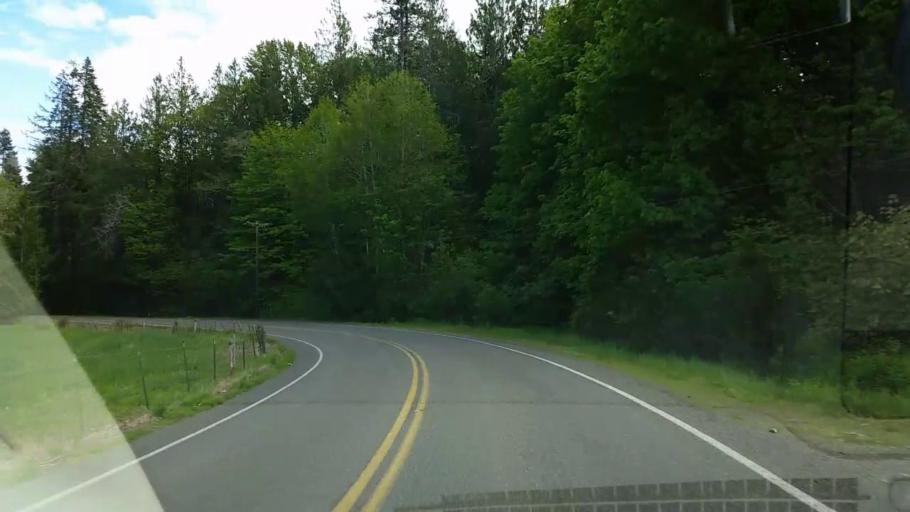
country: US
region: Washington
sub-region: Mason County
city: Shelton
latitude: 47.3164
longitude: -123.2575
